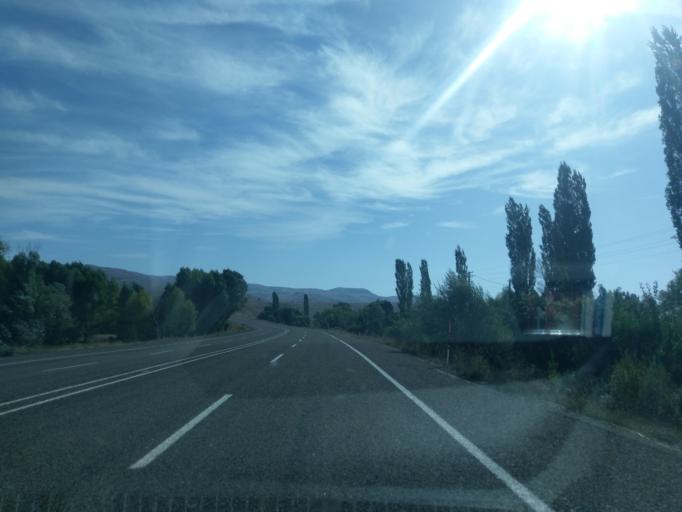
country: TR
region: Sivas
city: Imranli
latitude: 39.8354
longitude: 38.2631
